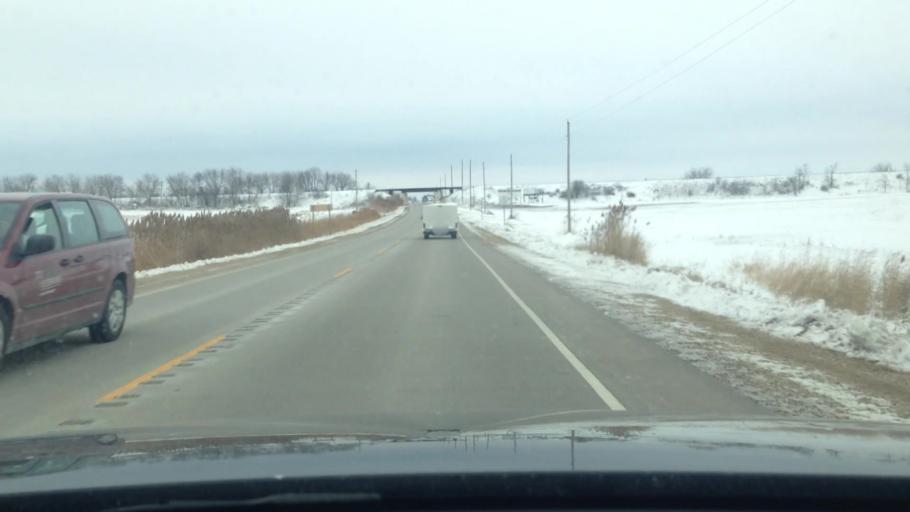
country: US
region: Illinois
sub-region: McHenry County
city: Hebron
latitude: 42.4965
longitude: -88.4423
